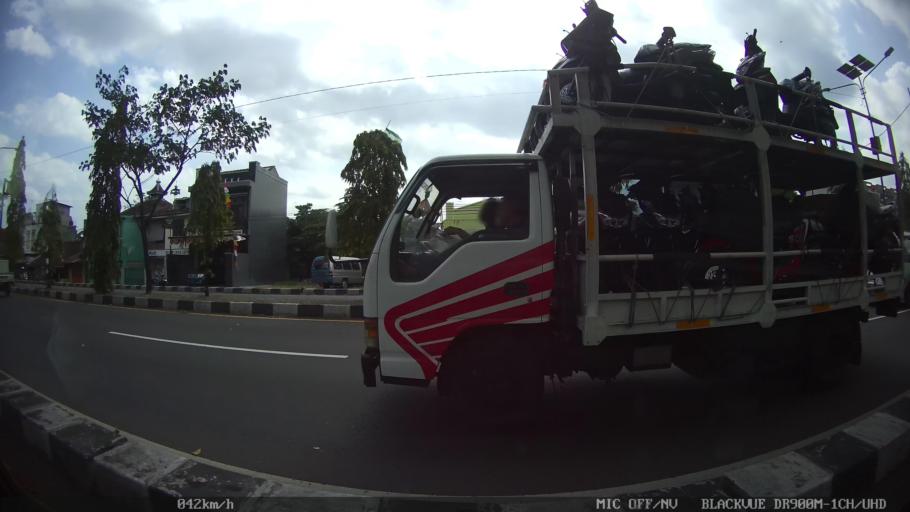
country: ID
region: Daerah Istimewa Yogyakarta
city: Gamping Lor
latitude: -7.7742
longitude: 110.3327
